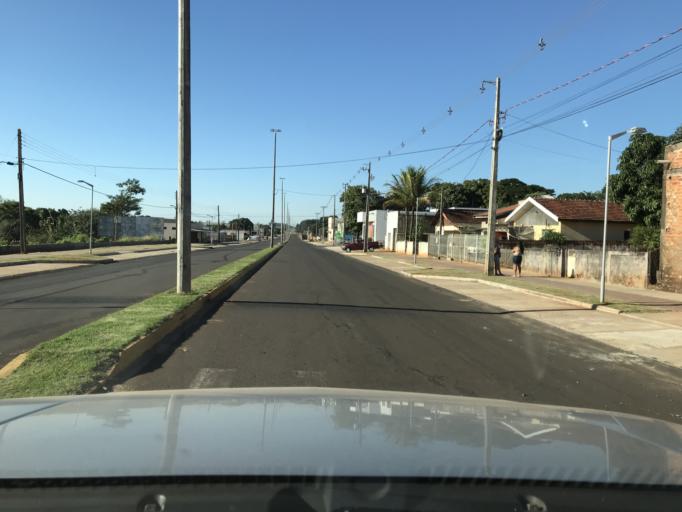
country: BR
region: Parana
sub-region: Ipora
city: Ipora
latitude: -24.0003
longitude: -53.7027
